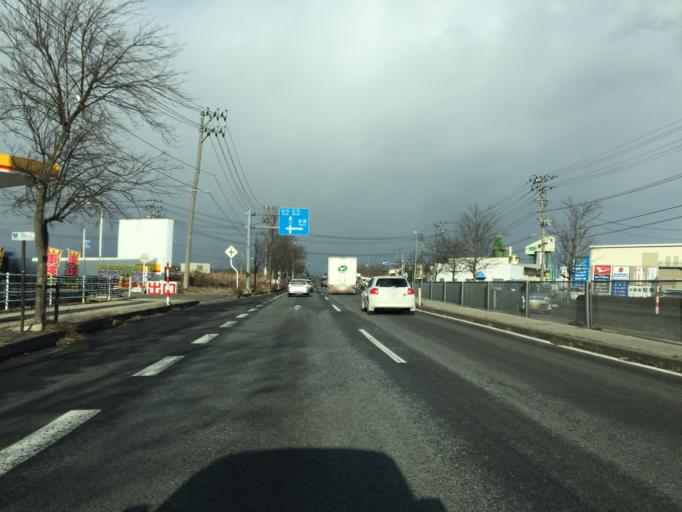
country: JP
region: Fukushima
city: Hobaramachi
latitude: 37.8297
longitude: 140.5136
